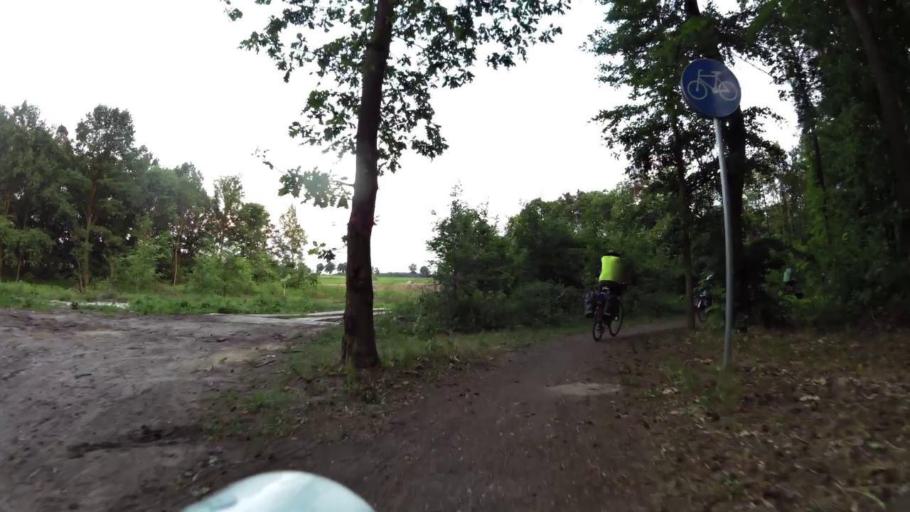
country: PL
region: Kujawsko-Pomorskie
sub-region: Powiat bydgoski
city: Dabrowa Chelminska
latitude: 53.1662
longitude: 18.2548
